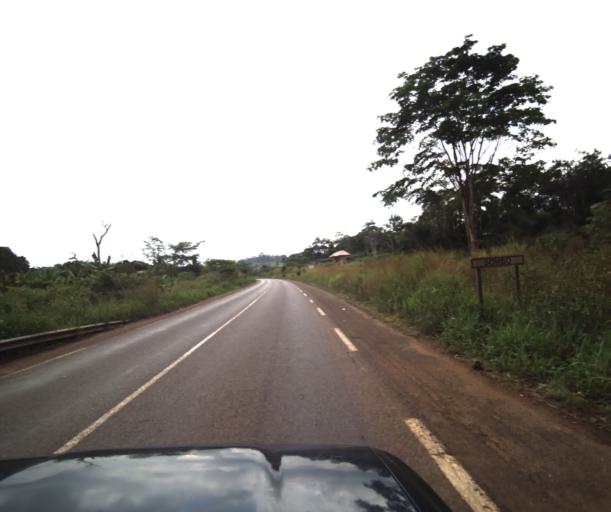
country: CM
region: Centre
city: Eseka
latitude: 3.8925
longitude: 10.7188
